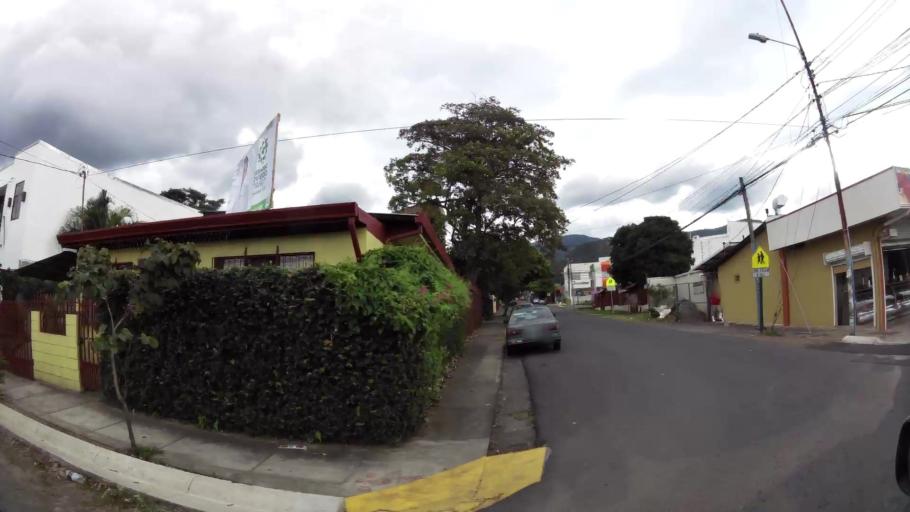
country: CR
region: San Jose
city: Santa Ana
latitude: 9.9338
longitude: -84.1827
